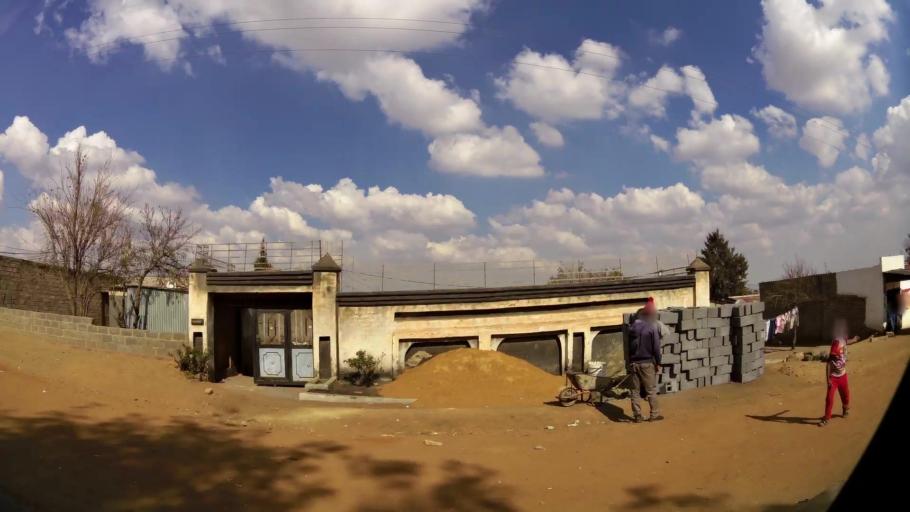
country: ZA
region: Gauteng
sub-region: City of Johannesburg Metropolitan Municipality
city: Roodepoort
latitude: -26.1900
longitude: 27.8655
